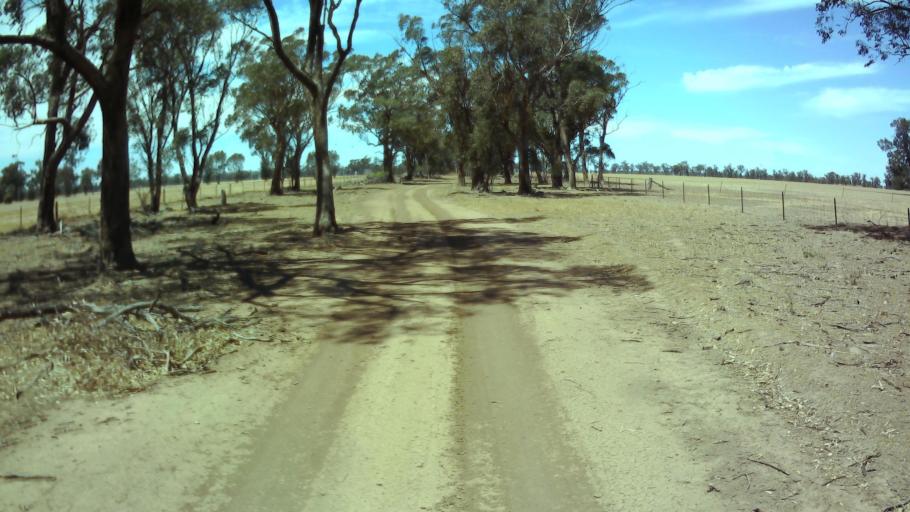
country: AU
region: New South Wales
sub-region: Weddin
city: Grenfell
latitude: -33.9201
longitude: 147.8048
